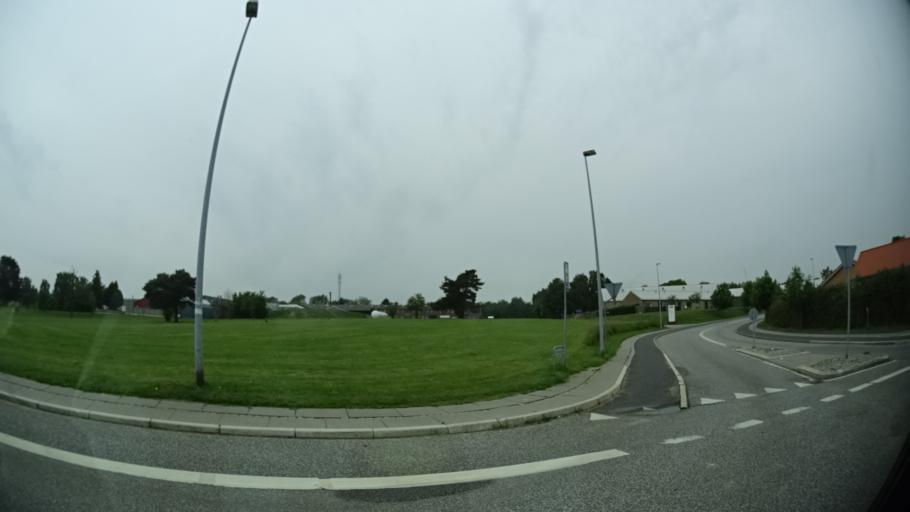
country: DK
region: Central Jutland
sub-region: Arhus Kommune
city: Logten
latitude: 56.2599
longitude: 10.3055
